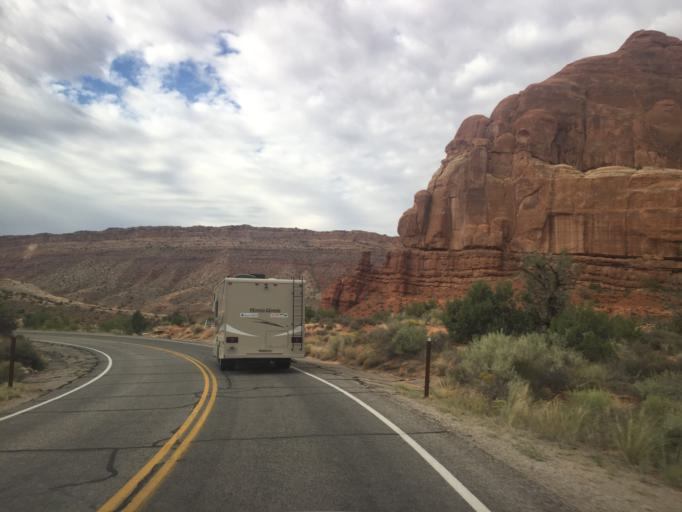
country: US
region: Utah
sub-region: Grand County
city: Moab
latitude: 38.6198
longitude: -109.6061
